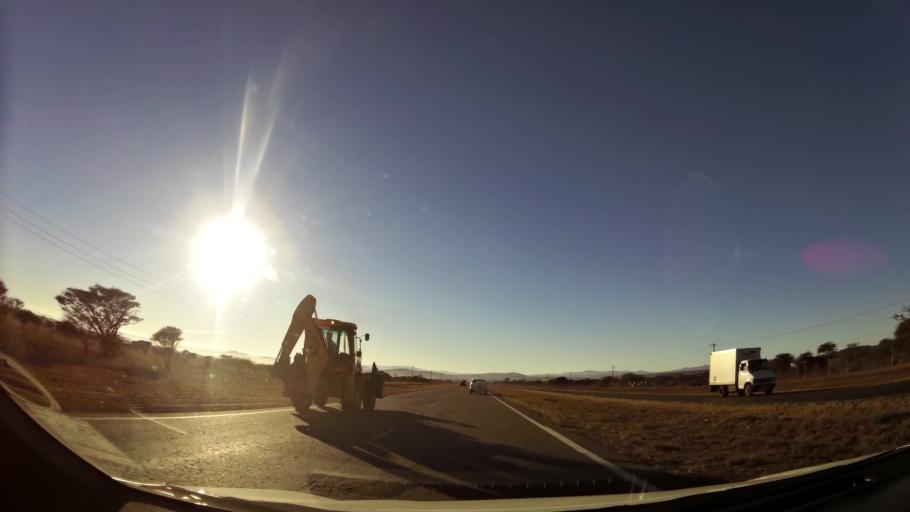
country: ZA
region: Limpopo
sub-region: Capricorn District Municipality
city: Polokwane
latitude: -23.8995
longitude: 29.5621
